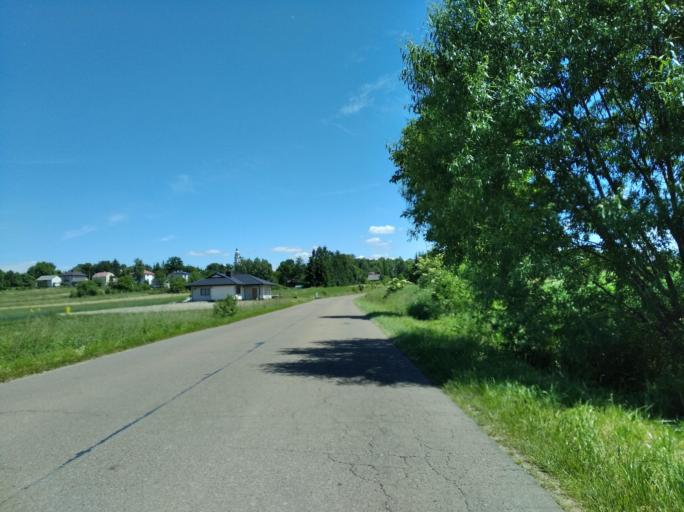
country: PL
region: Subcarpathian Voivodeship
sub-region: Powiat jasielski
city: Tarnowiec
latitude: 49.7265
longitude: 21.5691
